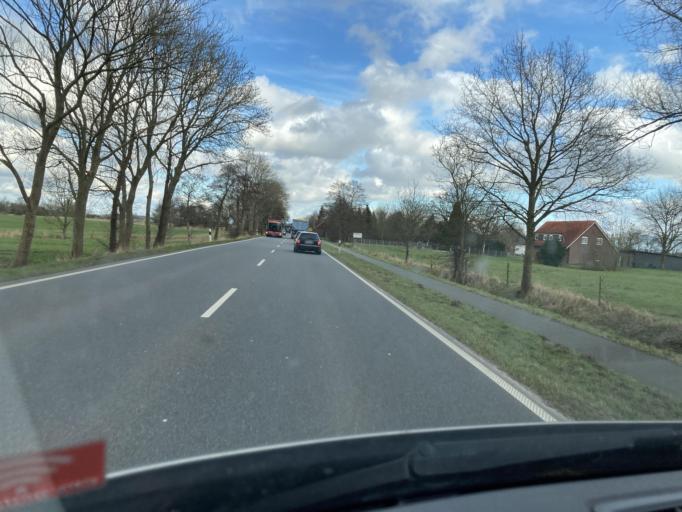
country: DE
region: Lower Saxony
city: Sande
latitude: 53.4775
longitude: 7.9671
